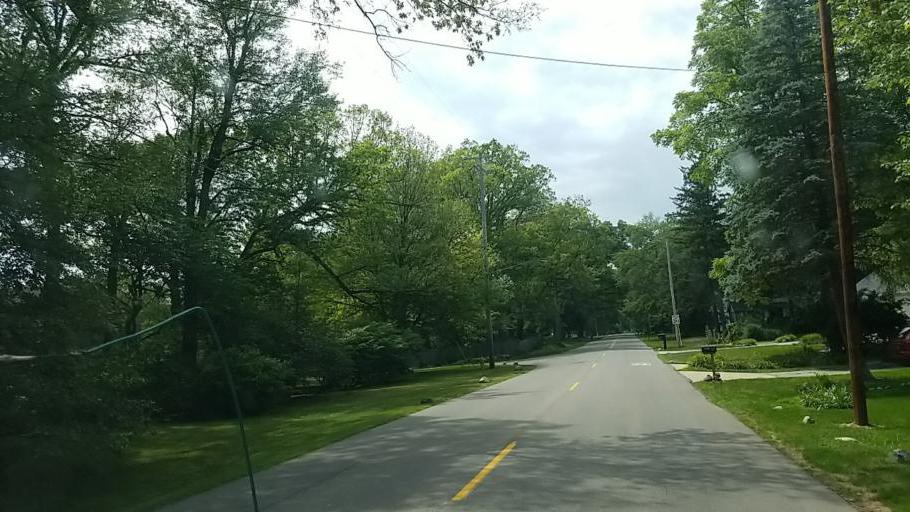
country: US
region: Michigan
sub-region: Kent County
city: Walker
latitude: 42.9933
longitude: -85.7205
